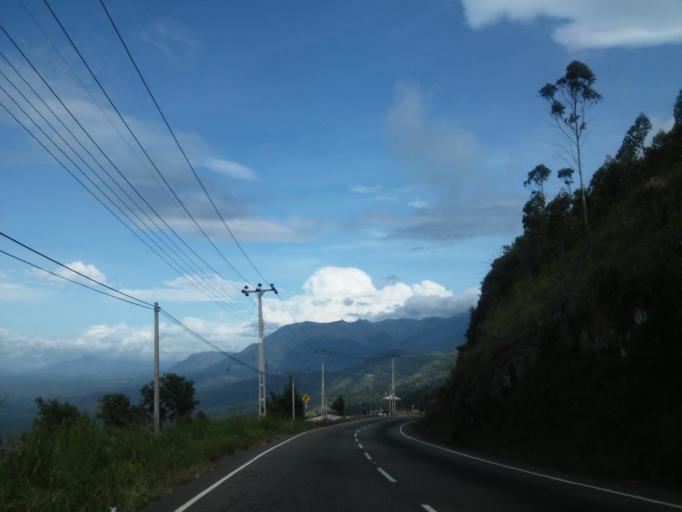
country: LK
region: Uva
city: Haputale
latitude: 6.7596
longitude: 80.9392
